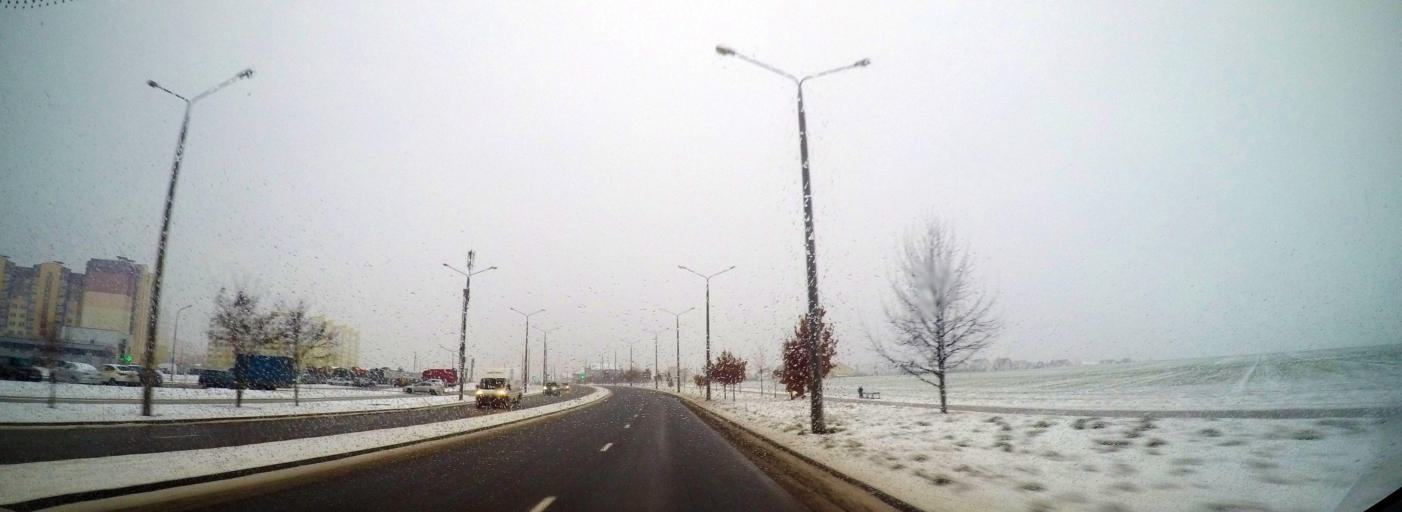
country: BY
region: Grodnenskaya
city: Hrodna
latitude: 53.6233
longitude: 23.8162
